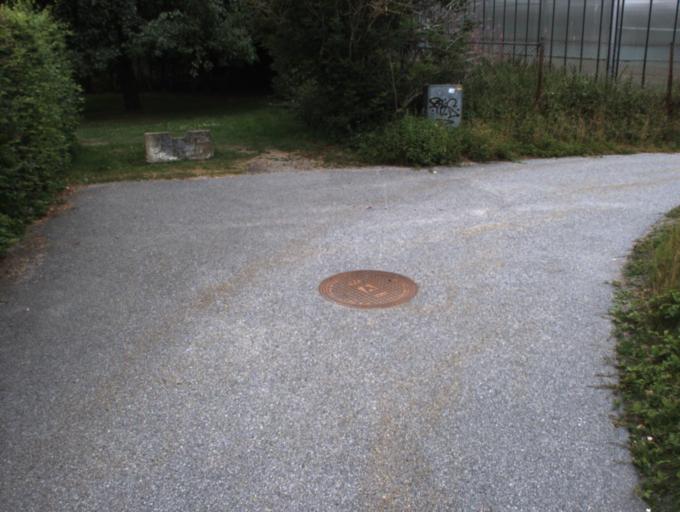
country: SE
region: Skane
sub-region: Helsingborg
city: Odakra
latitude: 56.0609
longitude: 12.7456
